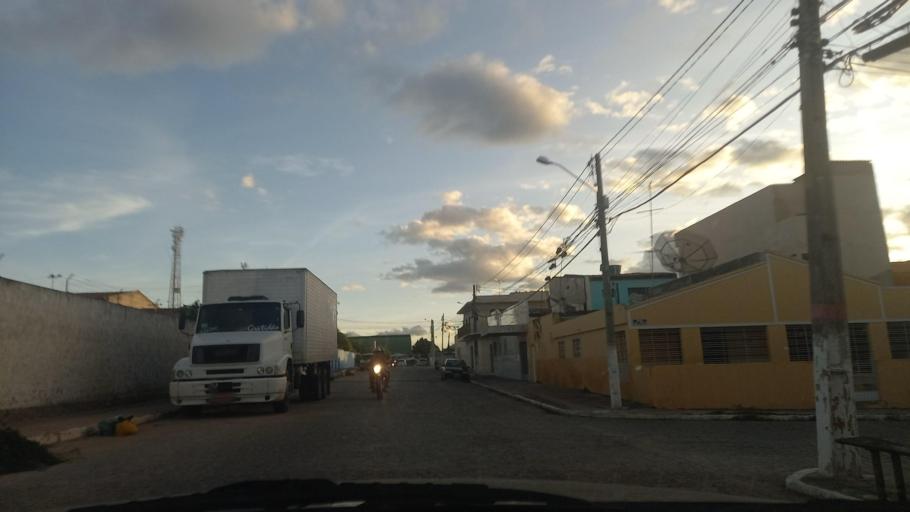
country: BR
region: Pernambuco
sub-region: Bezerros
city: Bezerros
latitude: -8.2406
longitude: -35.7517
